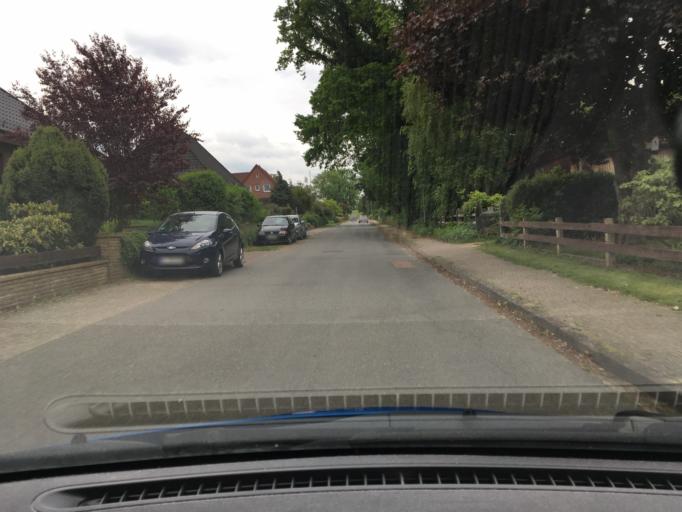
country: DE
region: Lower Saxony
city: Eyendorf
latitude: 53.2051
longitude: 10.1615
